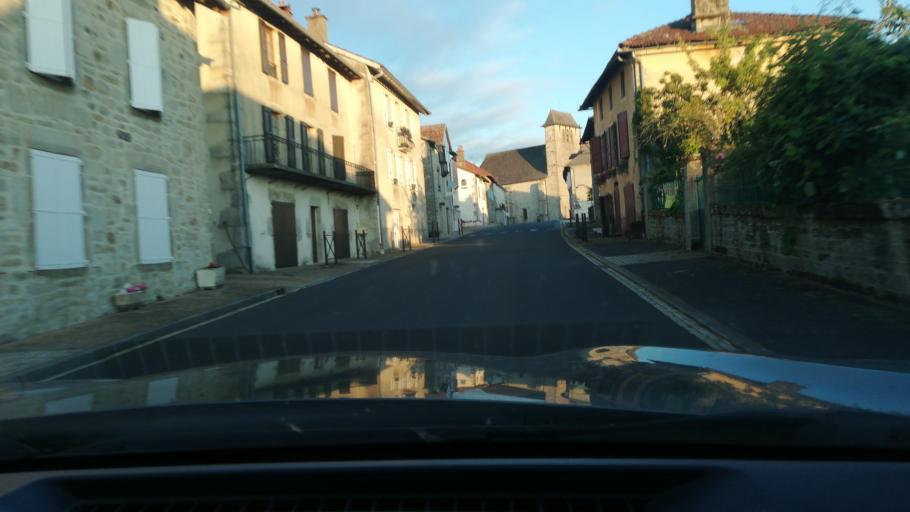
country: FR
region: Auvergne
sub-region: Departement du Cantal
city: Laroquebrou
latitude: 44.9554
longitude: 2.1260
